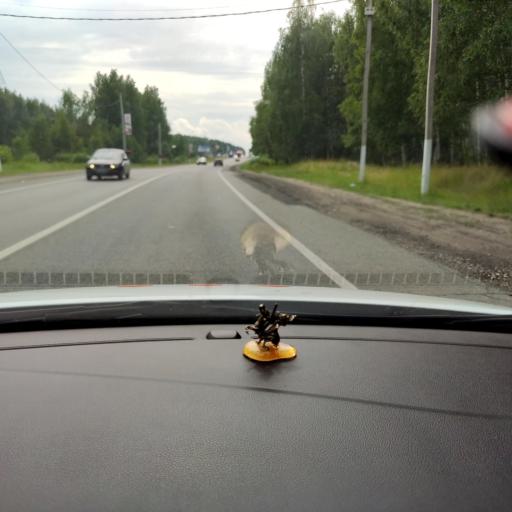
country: RU
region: Tatarstan
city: Aysha
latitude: 55.8594
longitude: 48.5823
